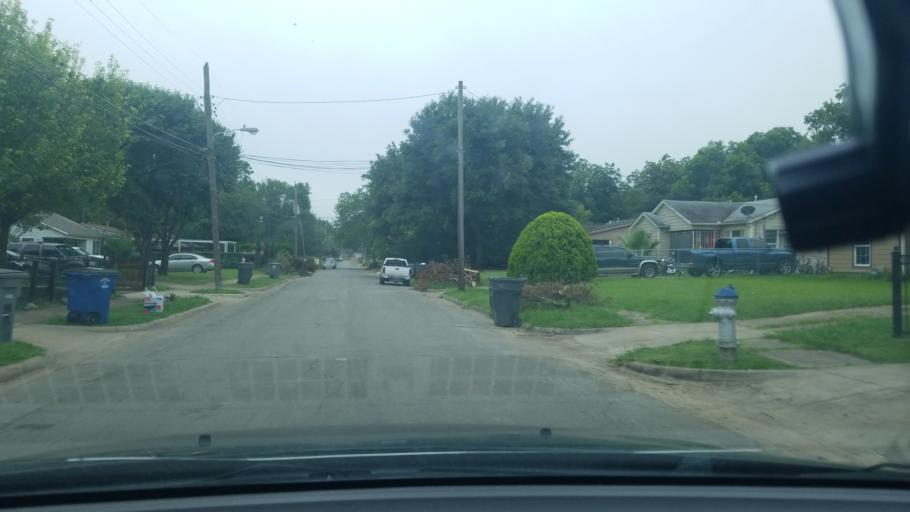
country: US
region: Texas
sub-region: Dallas County
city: Balch Springs
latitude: 32.7617
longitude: -96.6717
